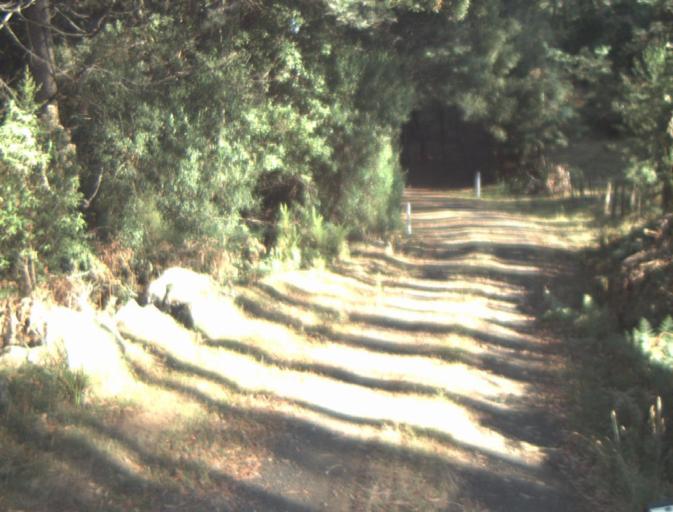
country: AU
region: Tasmania
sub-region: Launceston
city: Mayfield
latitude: -41.2847
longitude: 147.1878
